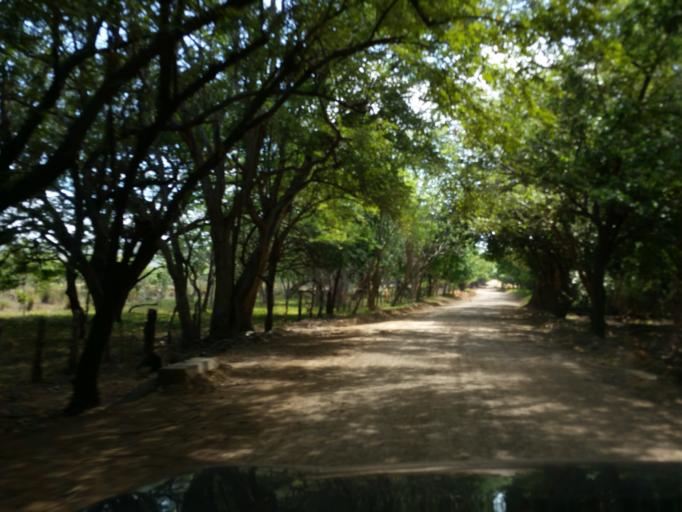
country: NI
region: Rivas
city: San Juan del Sur
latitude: 11.1421
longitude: -85.7868
